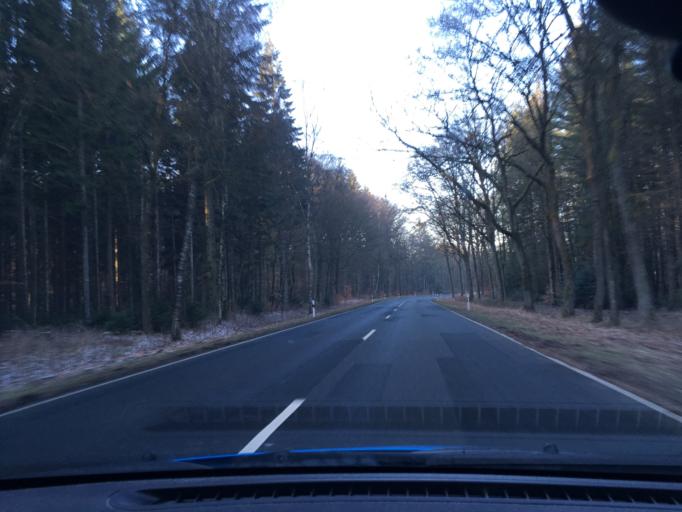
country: DE
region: Lower Saxony
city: Schneverdingen
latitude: 53.1567
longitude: 9.8441
